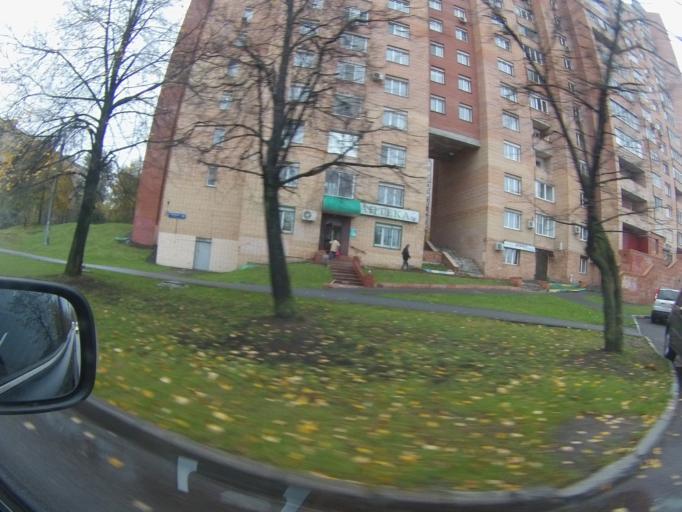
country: RU
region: Moskovskaya
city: Levoberezhnyy
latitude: 55.8504
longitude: 37.4820
